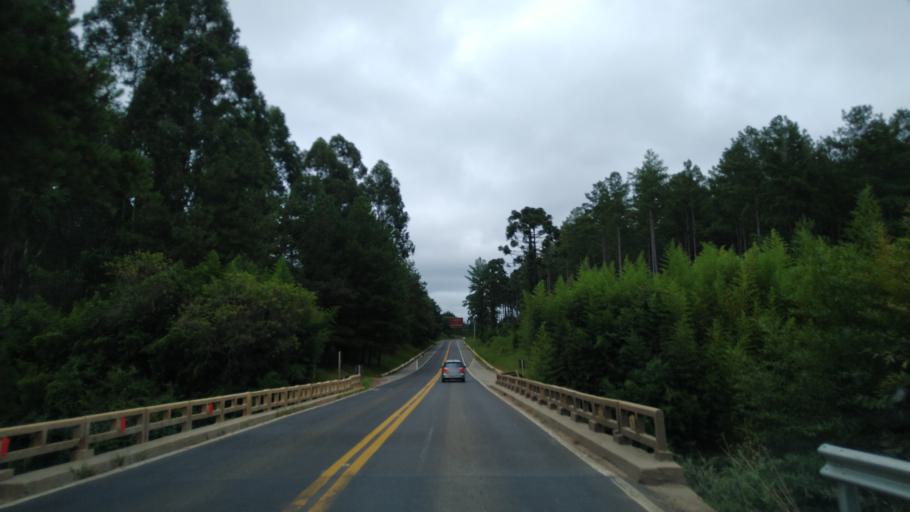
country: BR
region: Santa Catarina
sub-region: Tres Barras
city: Tres Barras
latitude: -26.1662
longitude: -50.1438
